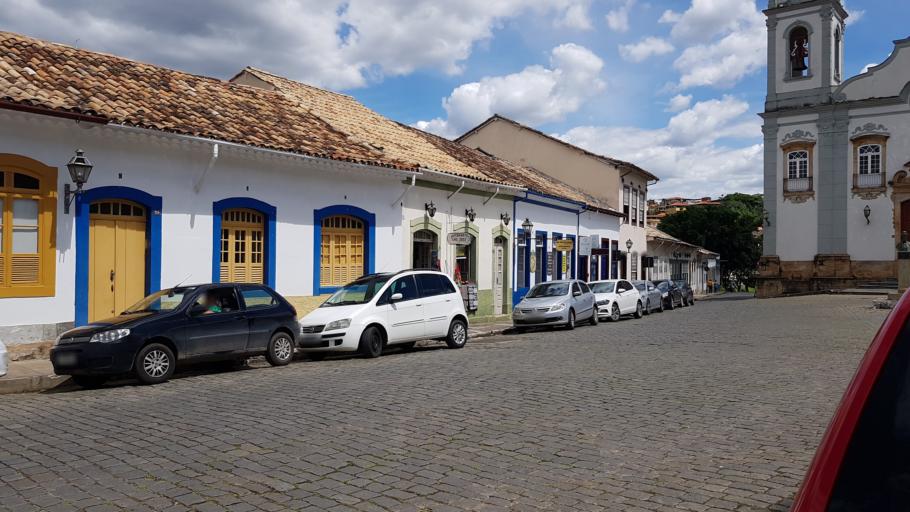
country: BR
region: Minas Gerais
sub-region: Sao Joao Del Rei
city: Sao Joao del Rei
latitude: -21.1360
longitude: -44.2624
